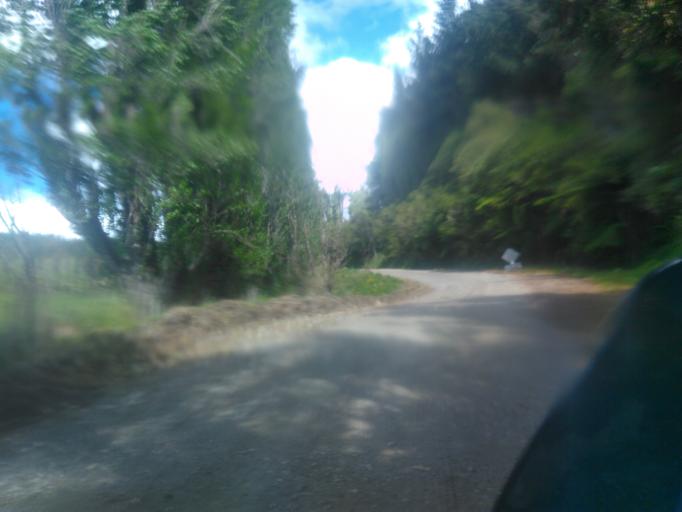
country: NZ
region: Hawke's Bay
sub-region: Wairoa District
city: Wairoa
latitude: -38.7683
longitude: 177.5954
